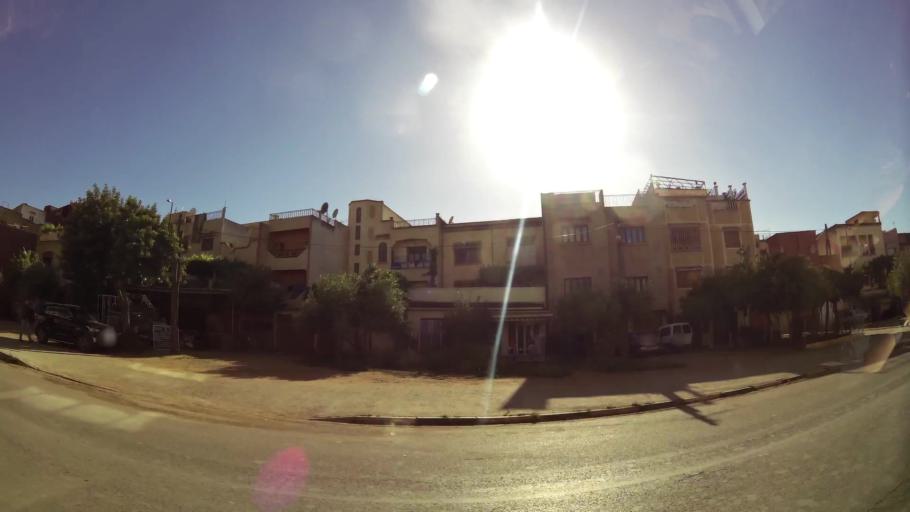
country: MA
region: Meknes-Tafilalet
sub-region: Meknes
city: Meknes
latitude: 33.8900
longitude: -5.5000
